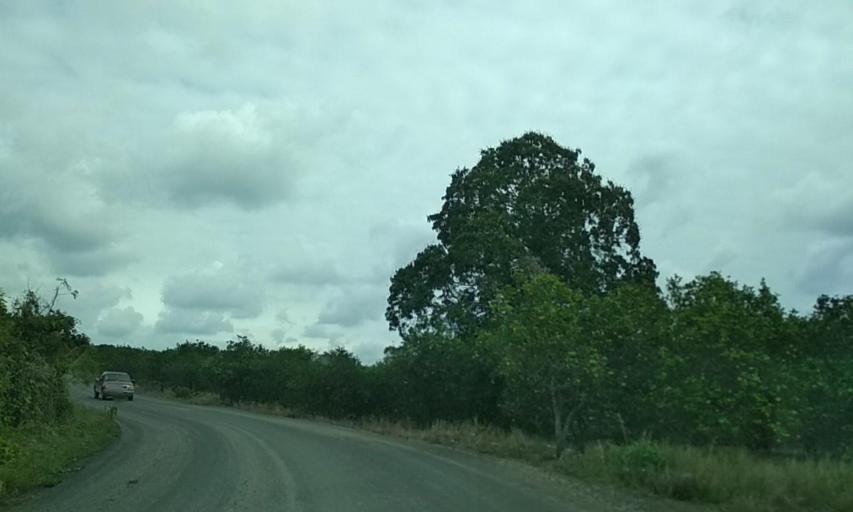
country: MX
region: Veracruz
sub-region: Papantla
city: El Chote
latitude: 20.3538
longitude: -97.3676
